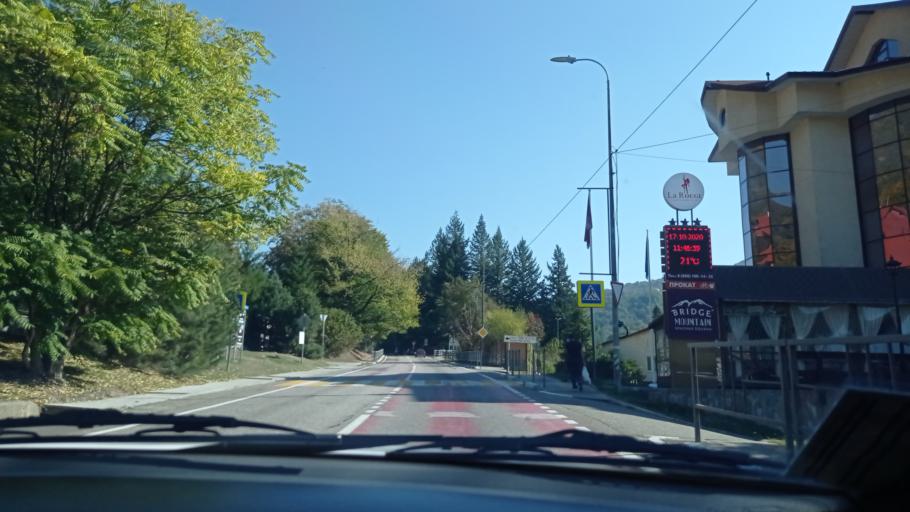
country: RU
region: Krasnodarskiy
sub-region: Sochi City
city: Krasnaya Polyana
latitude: 43.6826
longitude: 40.2172
